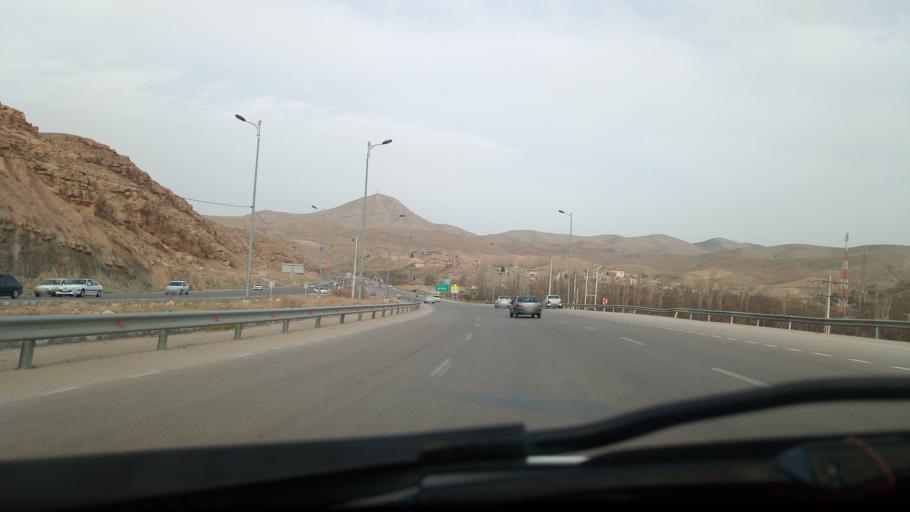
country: IR
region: Khorasan-e Shomali
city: Bojnurd
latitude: 37.4768
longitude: 57.4260
